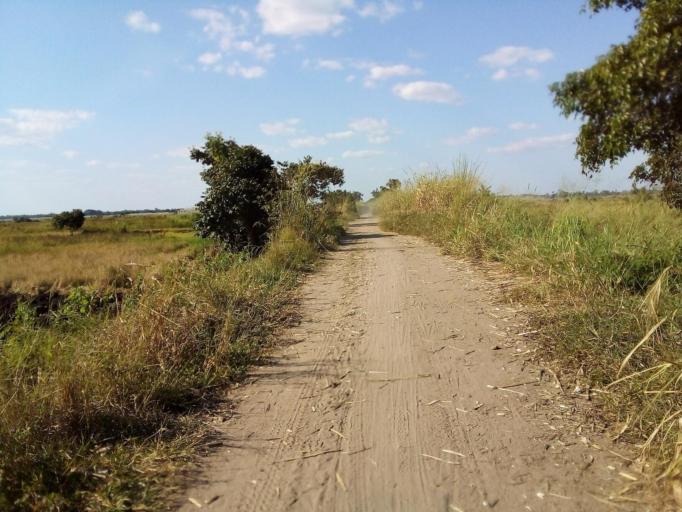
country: MZ
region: Zambezia
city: Quelimane
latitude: -17.5886
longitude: 36.8376
